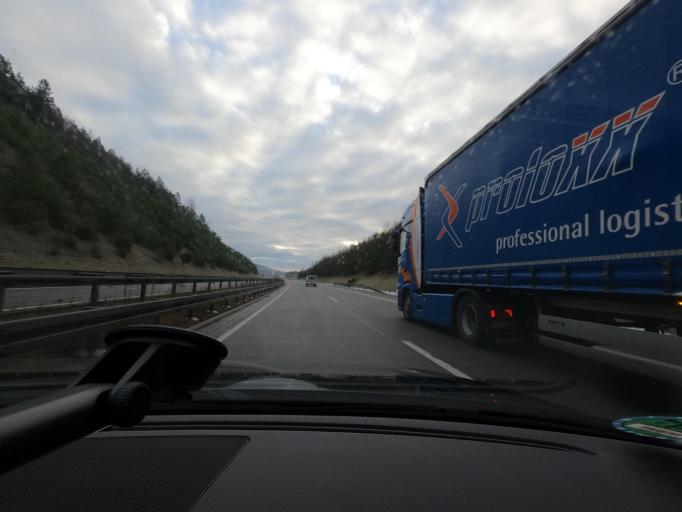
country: DE
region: Thuringia
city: Schleusingen
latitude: 50.4925
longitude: 10.8024
